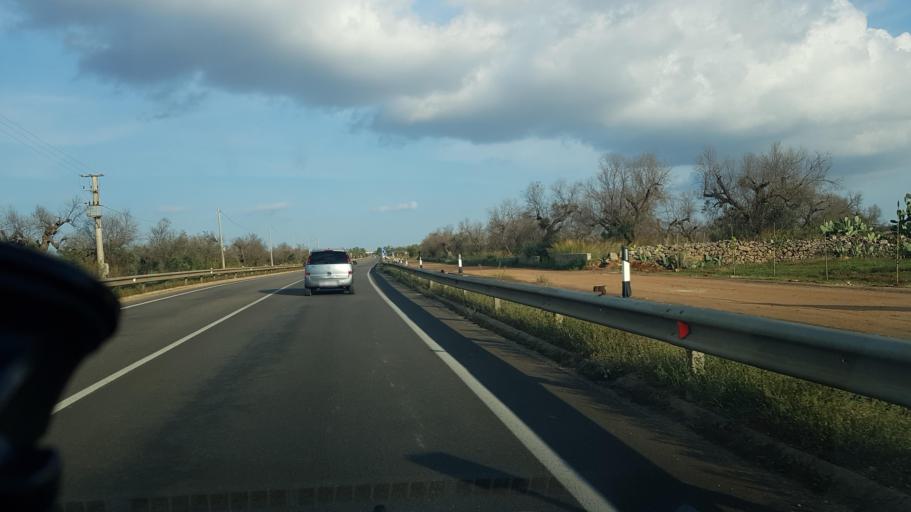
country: IT
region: Apulia
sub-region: Provincia di Lecce
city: Gemini
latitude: 39.9197
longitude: 18.2060
